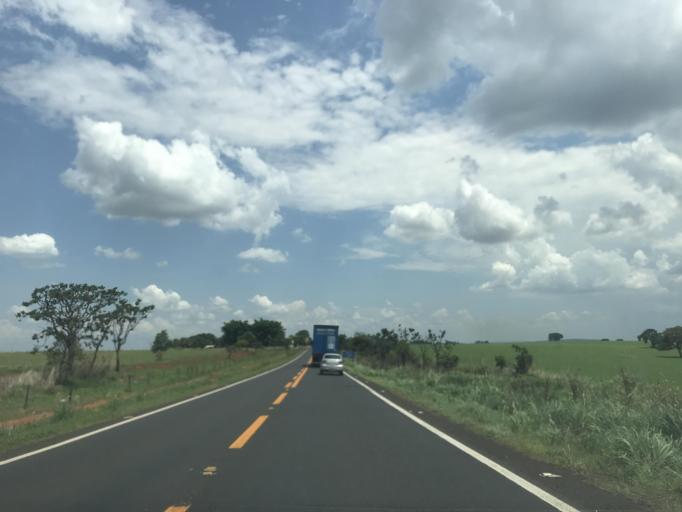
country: BR
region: Goias
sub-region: Piracanjuba
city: Piracanjuba
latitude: -17.4654
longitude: -48.7600
